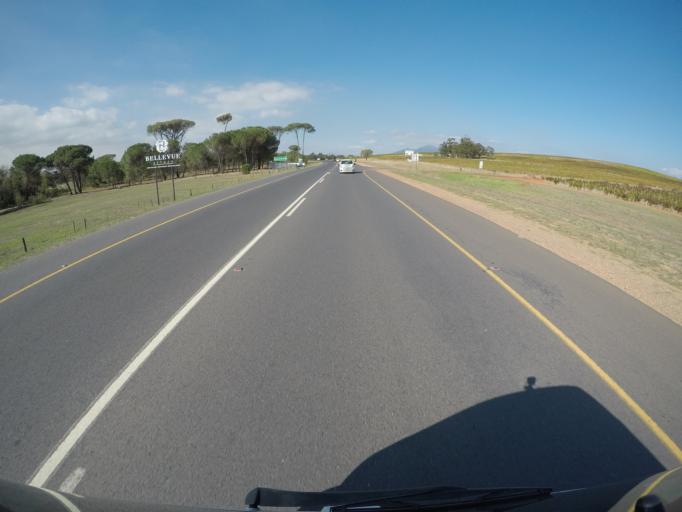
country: ZA
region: Western Cape
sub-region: City of Cape Town
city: Kraaifontein
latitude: -33.8805
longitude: 18.7628
